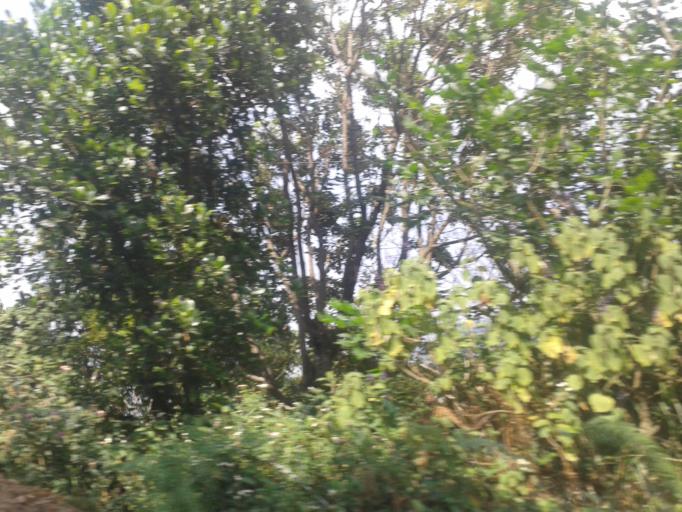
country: IN
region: Tamil Nadu
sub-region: Dindigul
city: Kodaikanal
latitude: 10.3238
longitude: 77.5659
